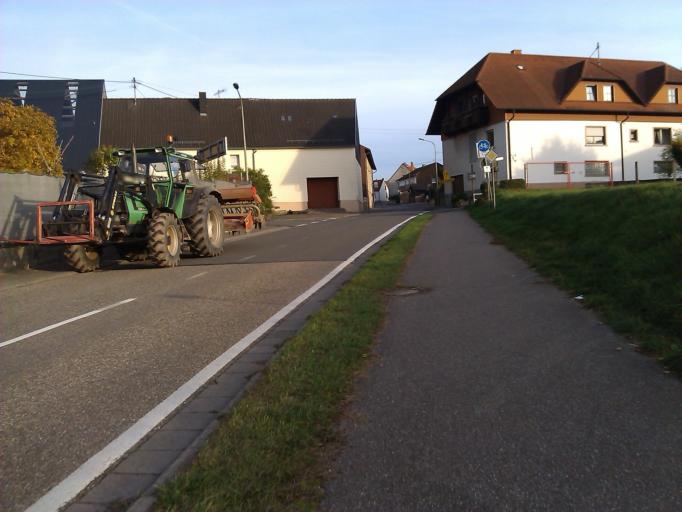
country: DE
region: Rheinland-Pfalz
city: Schallodenbach
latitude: 49.5448
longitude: 7.7130
